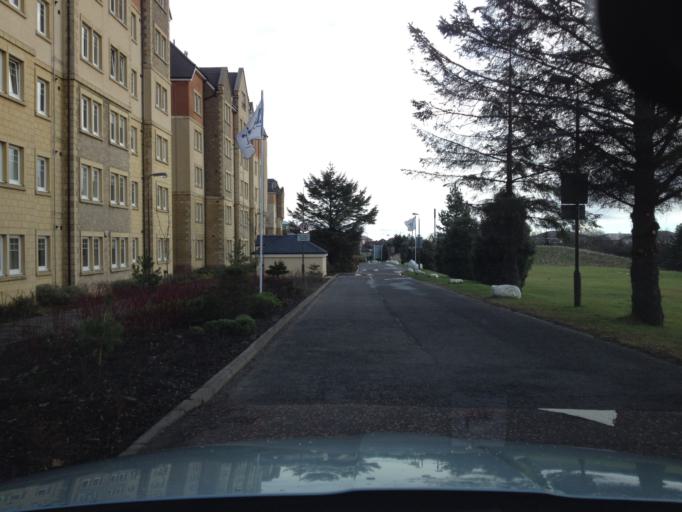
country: GB
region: Scotland
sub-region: West Lothian
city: Livingston
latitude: 55.9139
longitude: -3.5319
